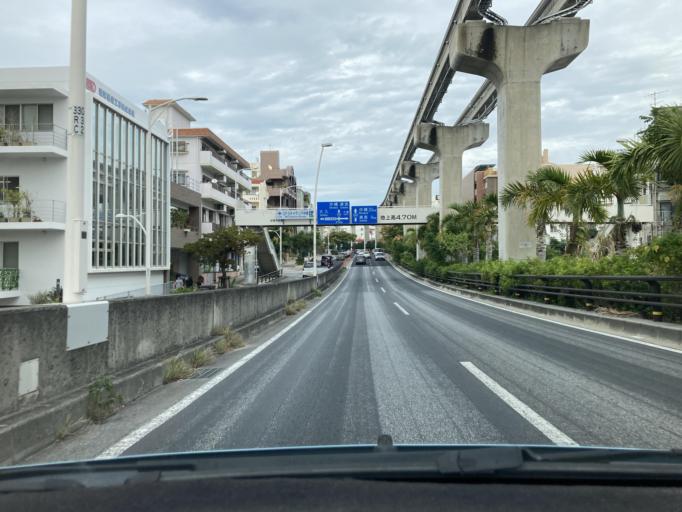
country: JP
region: Okinawa
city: Naha-shi
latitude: 26.2194
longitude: 127.6973
